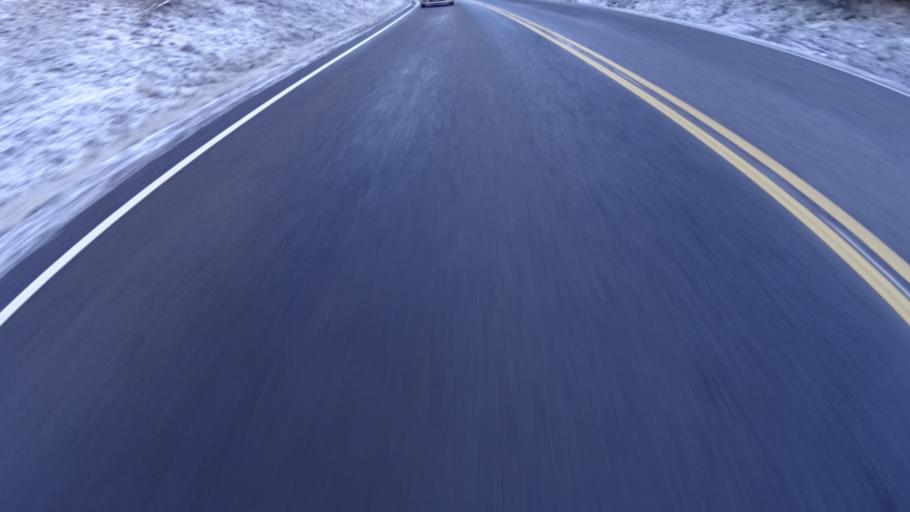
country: FI
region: Uusimaa
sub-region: Helsinki
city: Vihti
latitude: 60.5122
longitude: 24.4285
